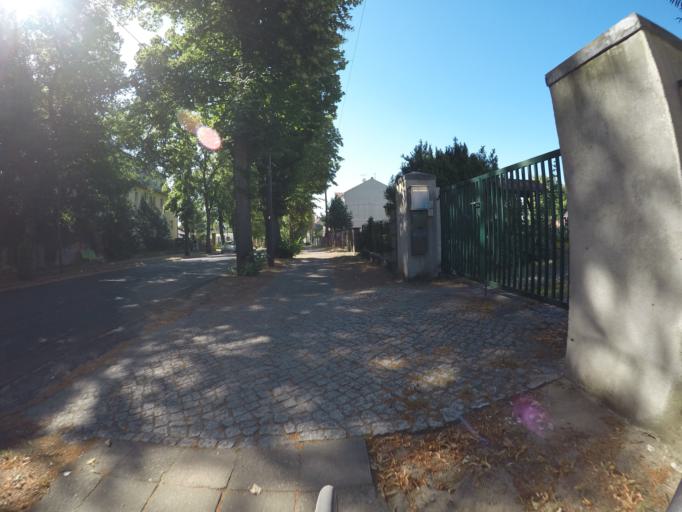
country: DE
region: Brandenburg
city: Woltersdorf
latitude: 52.4462
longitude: 13.7618
